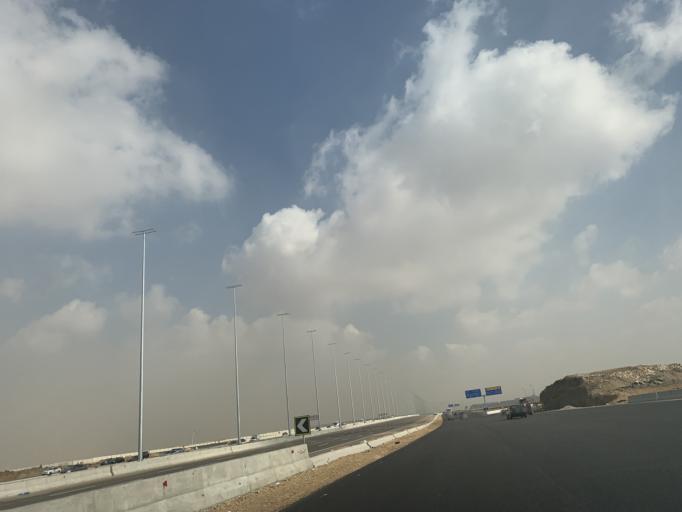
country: EG
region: Muhafazat al Qalyubiyah
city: Al Khankah
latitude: 30.0827
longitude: 31.4496
